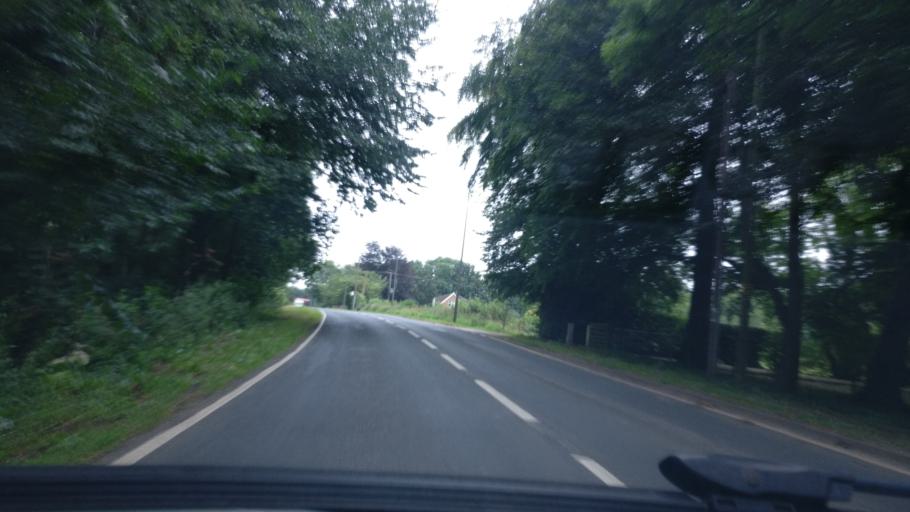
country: GB
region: England
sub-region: East Riding of Yorkshire
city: Leven
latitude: 53.8835
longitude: -0.3131
